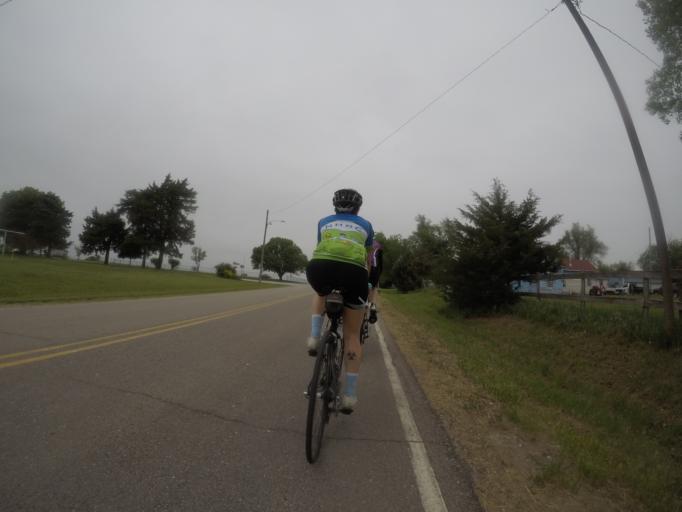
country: US
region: Kansas
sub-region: Pottawatomie County
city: Westmoreland
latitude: 39.5032
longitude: -96.3142
